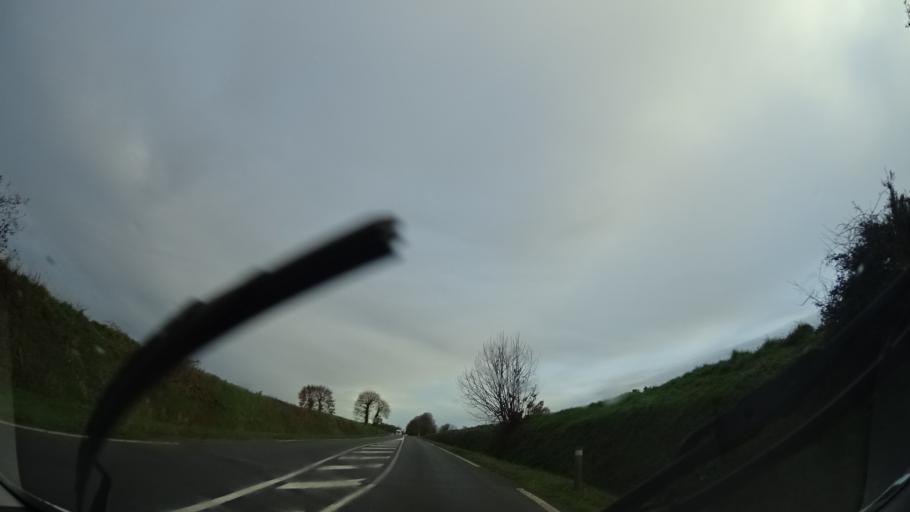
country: FR
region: Brittany
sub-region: Departement des Cotes-d'Armor
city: Evran
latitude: 48.3892
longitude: -1.9797
